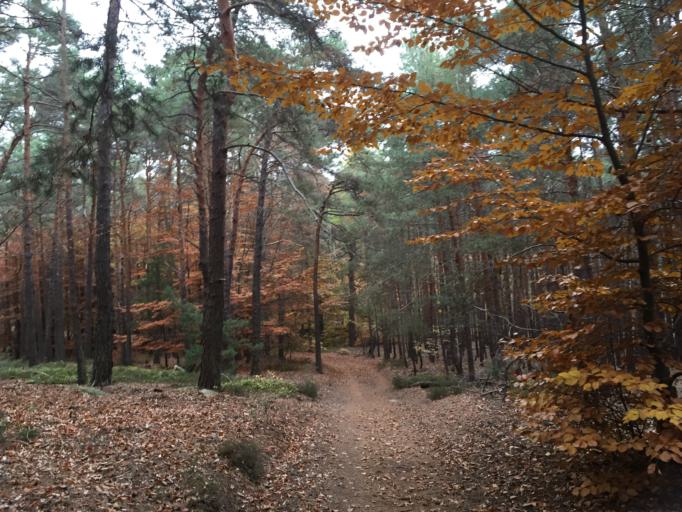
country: DE
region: Rheinland-Pfalz
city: Deidesheim
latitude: 49.4171
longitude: 8.1625
